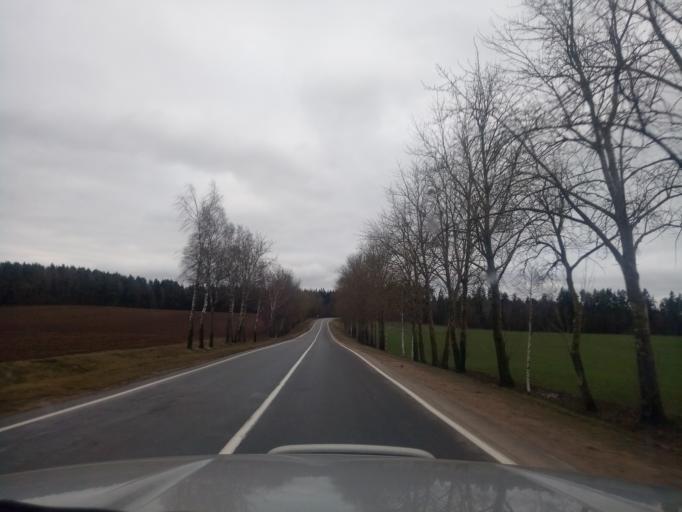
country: BY
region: Minsk
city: Kapyl'
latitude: 53.1670
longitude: 27.1235
